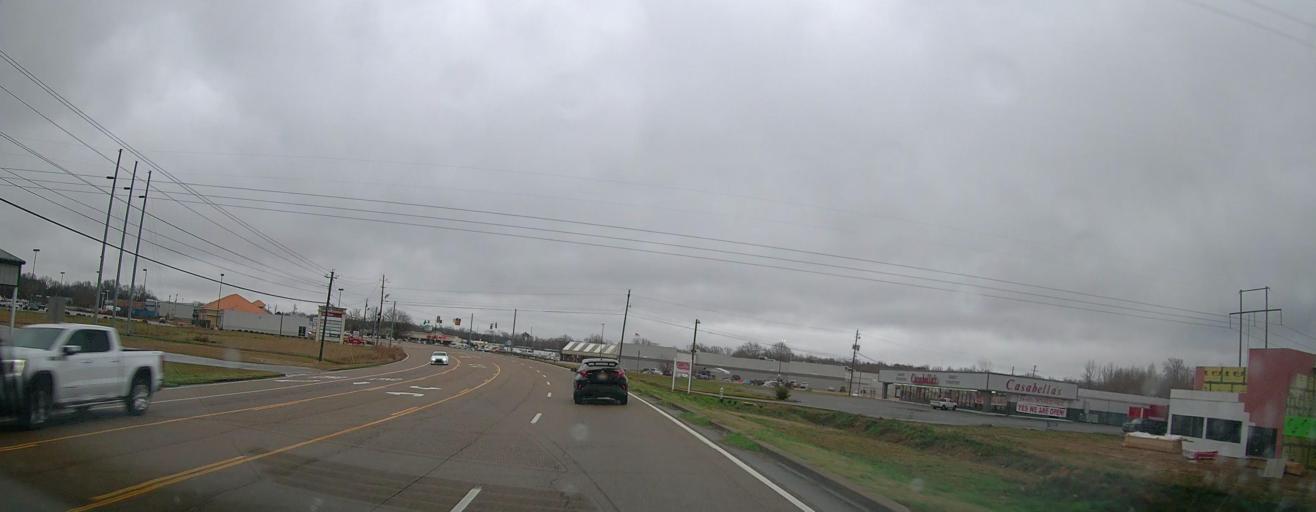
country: US
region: Mississippi
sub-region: Alcorn County
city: Corinth
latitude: 34.9097
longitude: -88.5055
